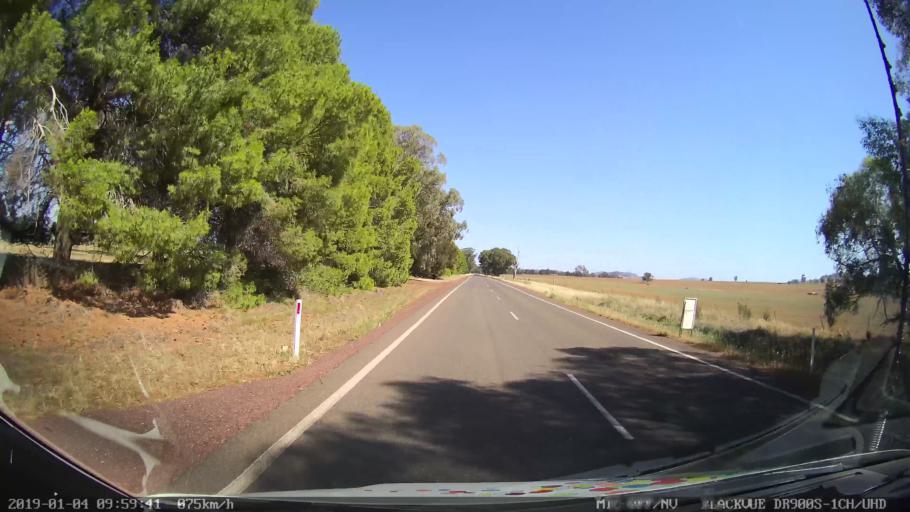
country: AU
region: New South Wales
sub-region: Cabonne
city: Canowindra
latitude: -33.5052
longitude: 148.3846
